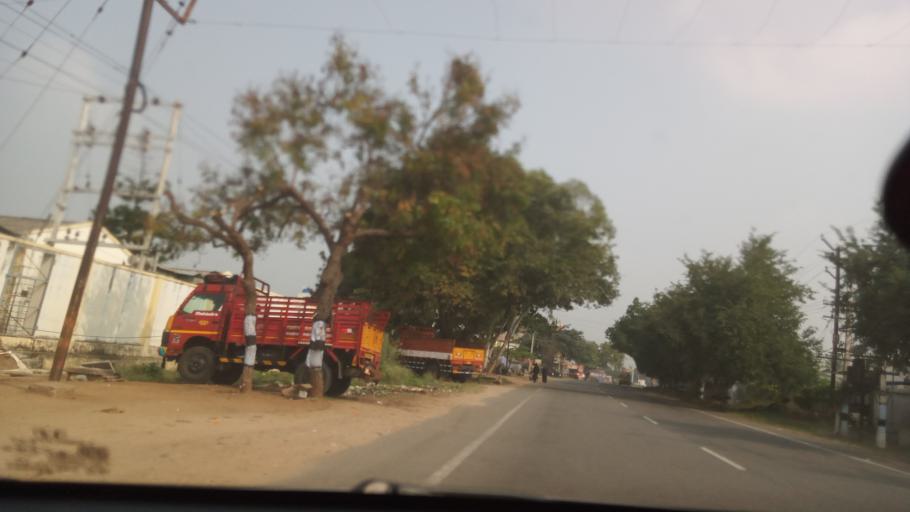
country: IN
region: Tamil Nadu
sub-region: Erode
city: Punjai Puliyampatti
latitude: 11.3602
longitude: 77.1698
